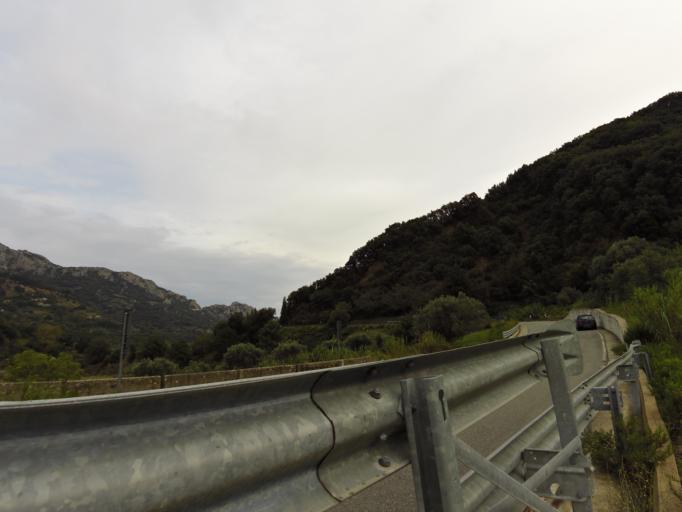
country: IT
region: Calabria
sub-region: Provincia di Reggio Calabria
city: Pazzano
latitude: 38.4430
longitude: 16.3993
